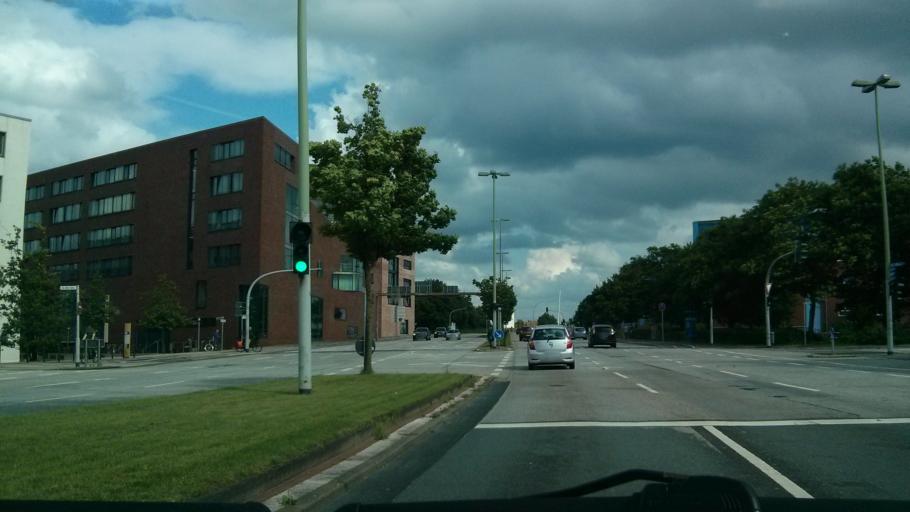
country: DE
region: Bremen
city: Bremerhaven
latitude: 53.5399
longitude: 8.5803
